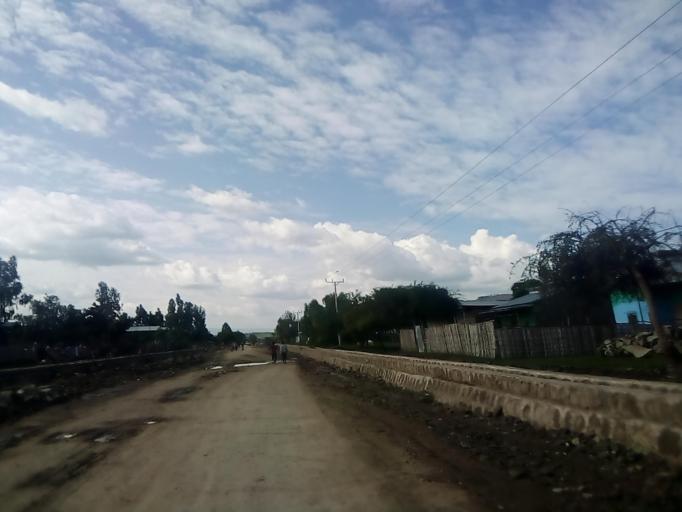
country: ET
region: Southern Nations, Nationalities, and People's Region
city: K'olito
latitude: 7.5999
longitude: 38.0669
